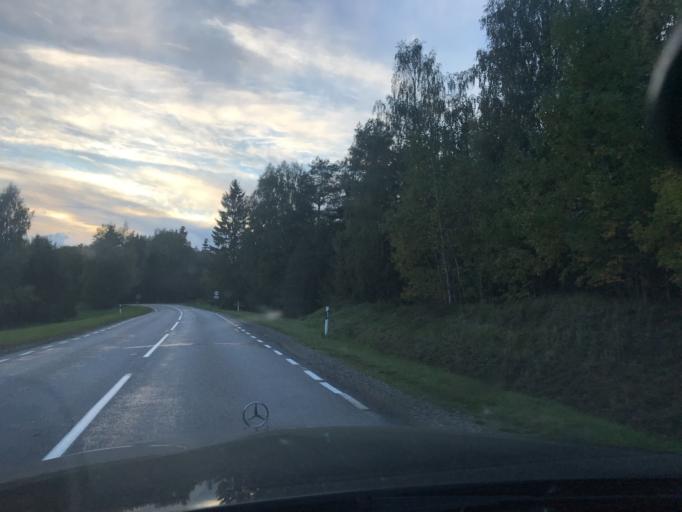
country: EE
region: Valgamaa
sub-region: Torva linn
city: Torva
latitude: 58.0071
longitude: 26.0895
